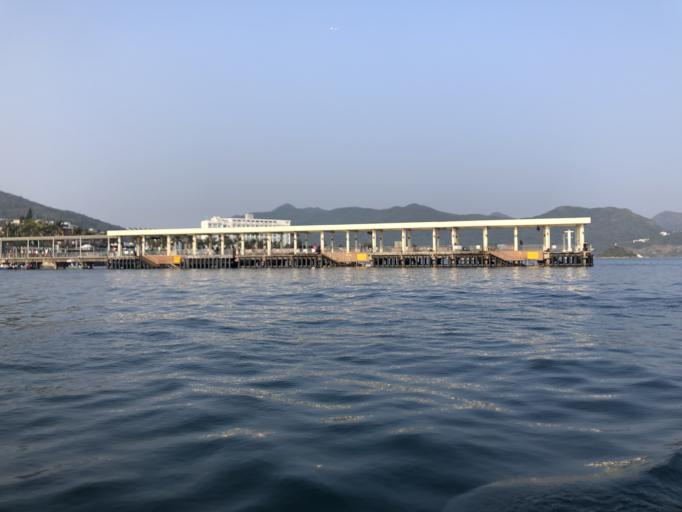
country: HK
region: Sai Kung
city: Sai Kung
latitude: 22.3806
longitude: 114.2752
